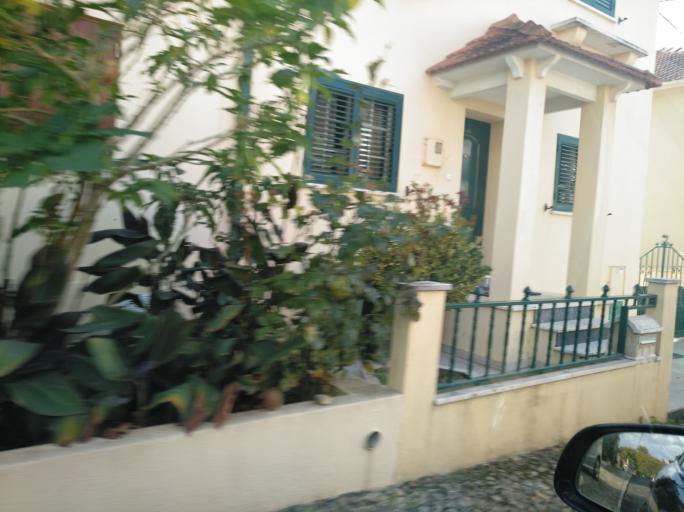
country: PT
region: Lisbon
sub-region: Loures
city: Moscavide
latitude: 38.7704
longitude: -9.1162
